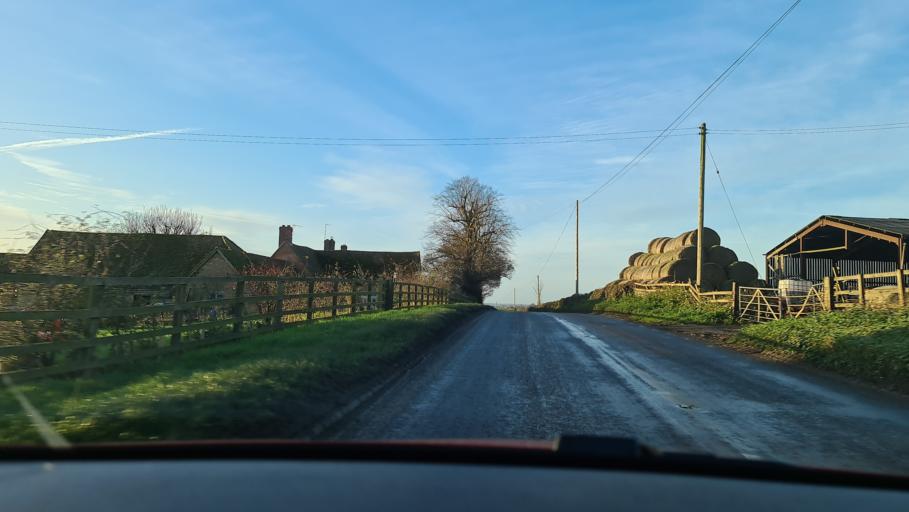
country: GB
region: England
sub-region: Buckinghamshire
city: Waddesdon
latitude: 51.8186
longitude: -0.9260
